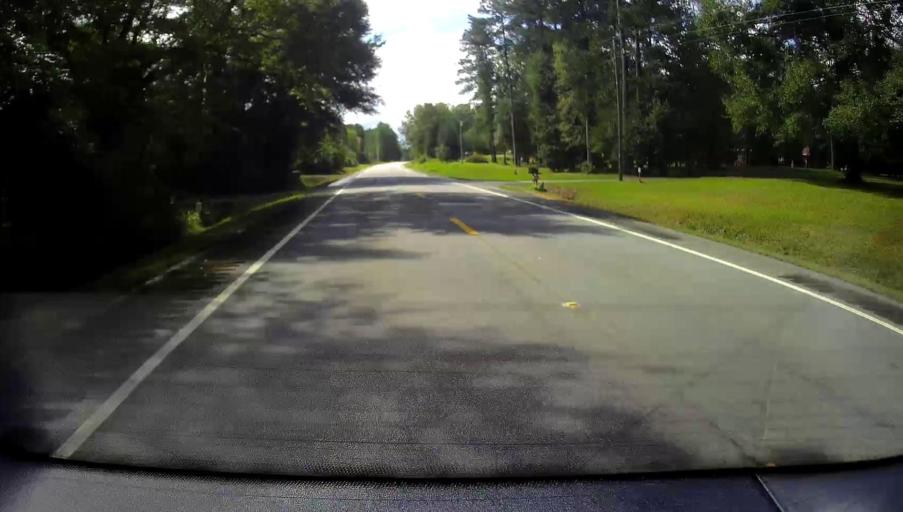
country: US
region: Georgia
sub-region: Baldwin County
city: Milledgeville
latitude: 33.0327
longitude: -83.3160
